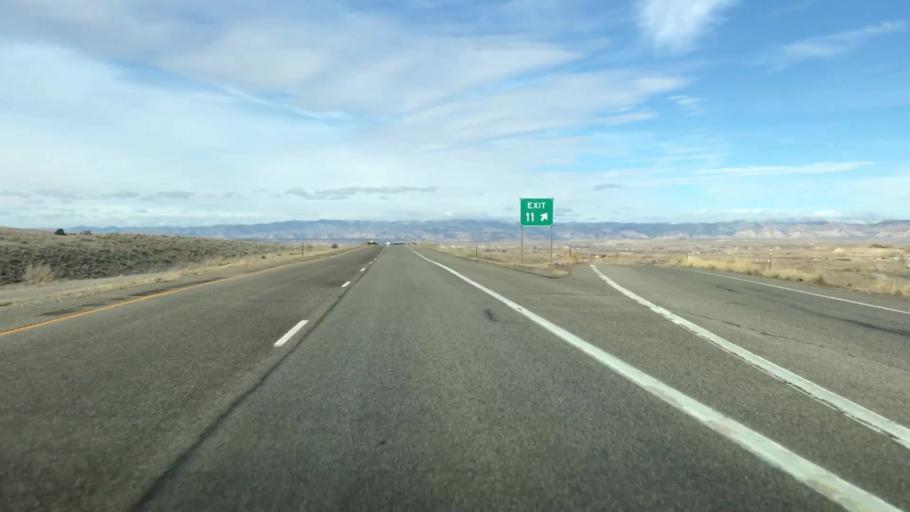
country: US
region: Colorado
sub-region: Mesa County
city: Loma
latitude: 39.2122
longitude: -108.8651
